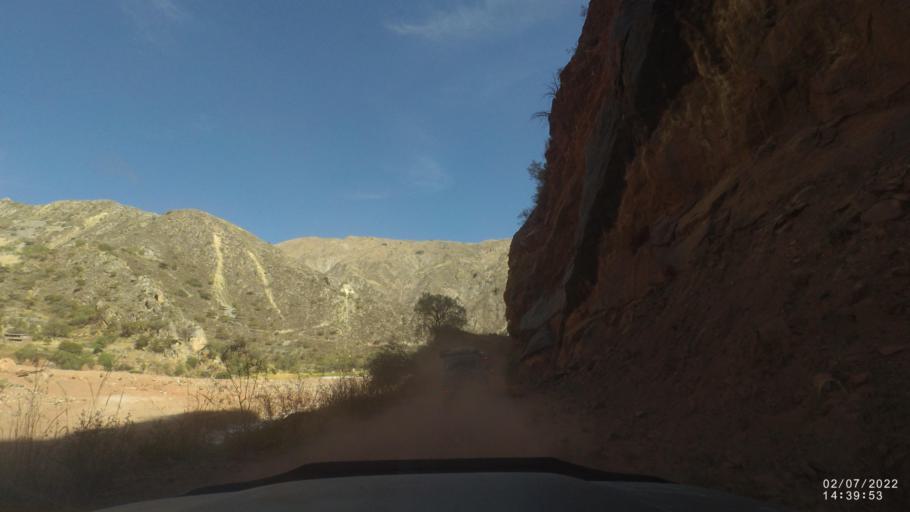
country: BO
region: Cochabamba
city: Irpa Irpa
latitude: -17.8481
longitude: -66.4201
